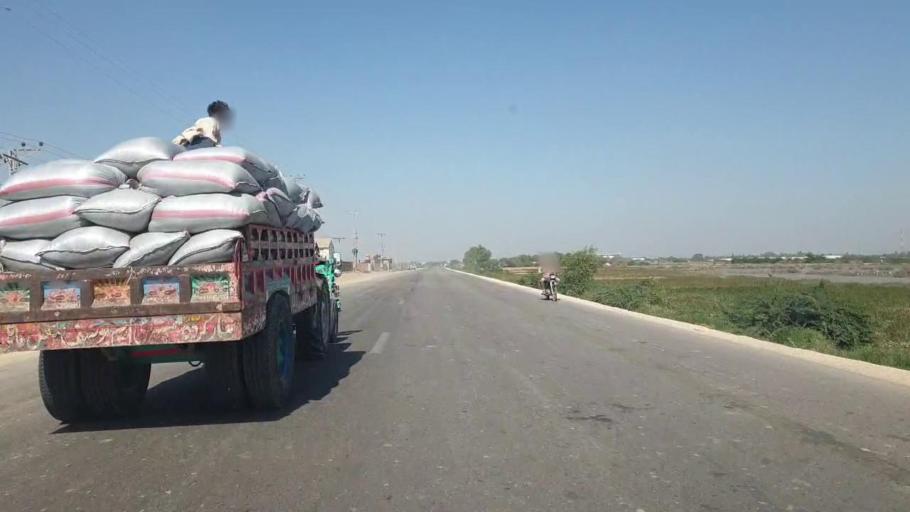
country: PK
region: Sindh
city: Talhar
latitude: 24.8667
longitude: 68.8168
